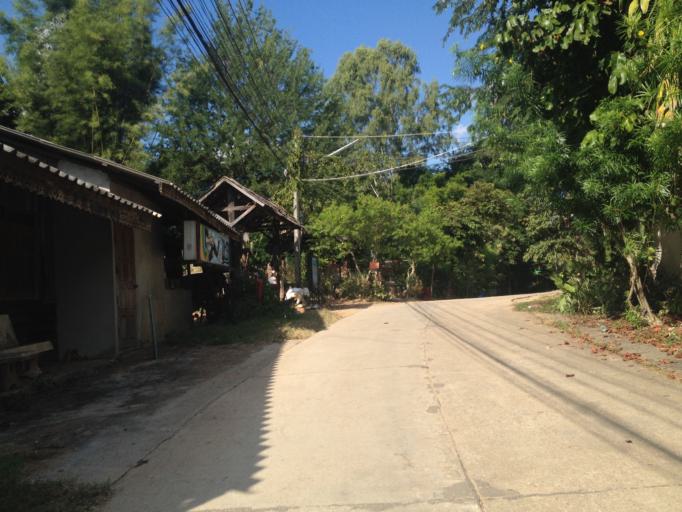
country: TH
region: Chiang Mai
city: Chiang Mai
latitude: 18.7787
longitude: 98.9477
